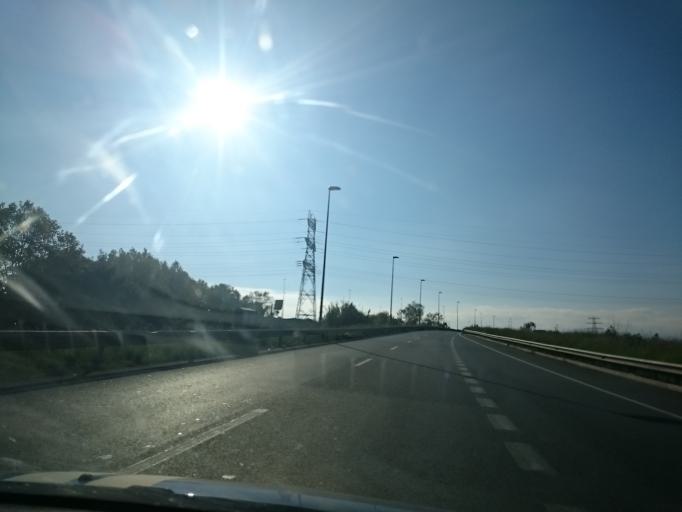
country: ES
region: Catalonia
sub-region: Provincia de Barcelona
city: El Prat de Llobregat
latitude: 41.3421
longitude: 2.1042
